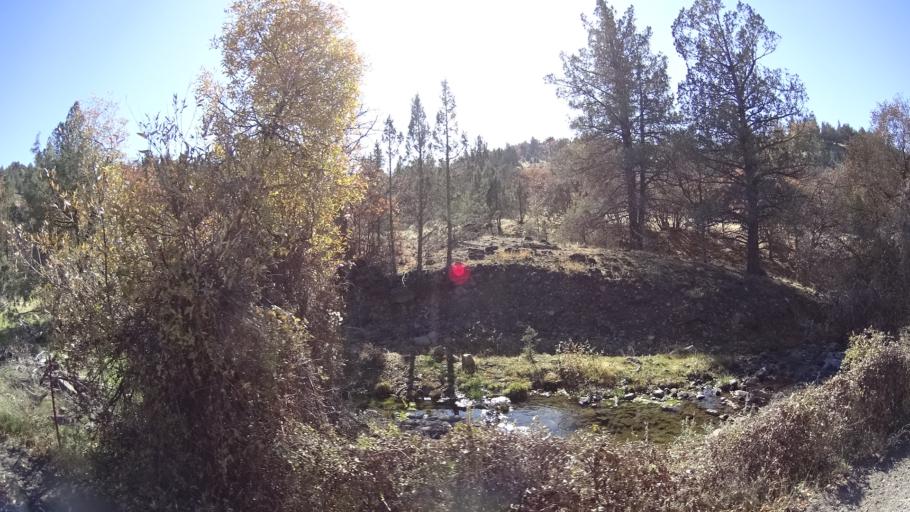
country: US
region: California
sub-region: Siskiyou County
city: Montague
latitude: 41.7926
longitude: -122.3530
